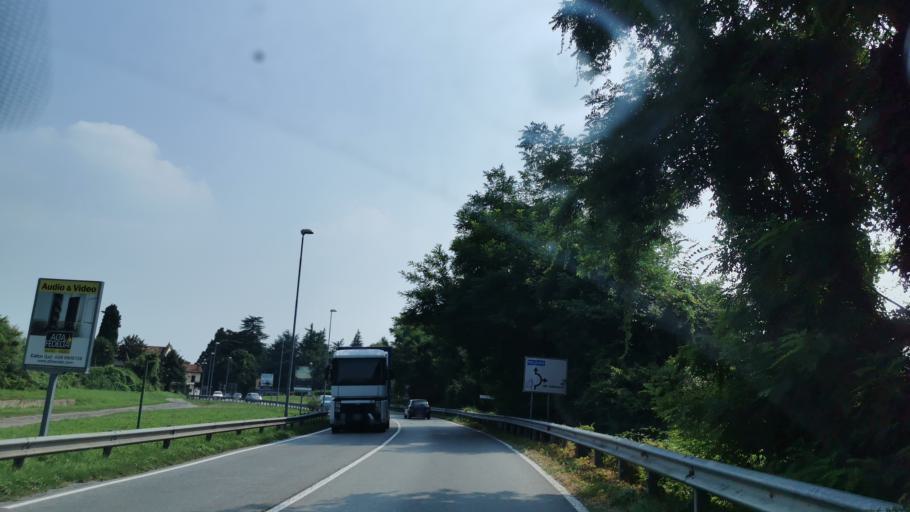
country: IT
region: Lombardy
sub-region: Provincia di Lecco
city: Canova-San Zeno
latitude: 45.7125
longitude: 9.4062
